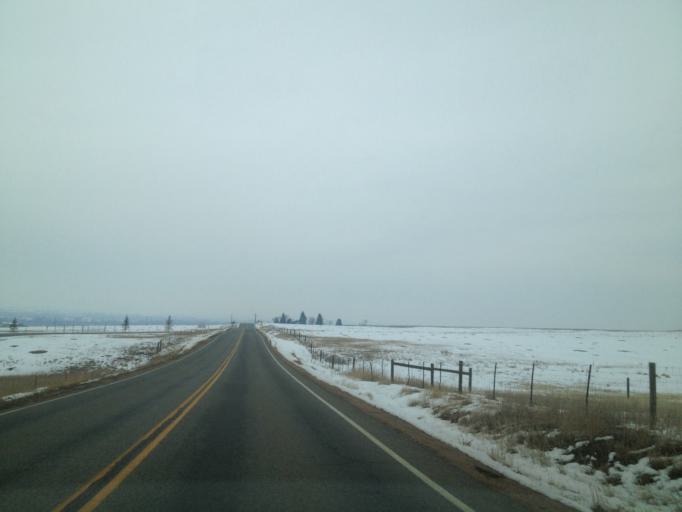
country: US
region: Colorado
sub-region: Boulder County
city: Gunbarrel
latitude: 40.0749
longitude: -105.1691
